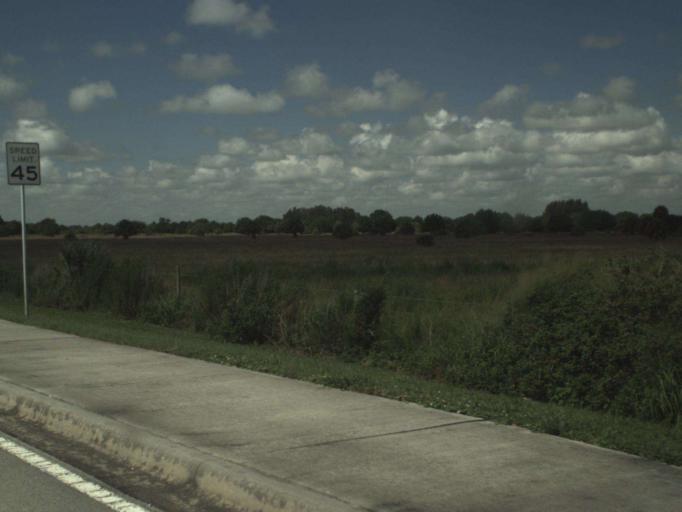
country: US
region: Florida
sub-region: Indian River County
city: Vero Beach South
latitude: 27.5939
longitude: -80.4474
